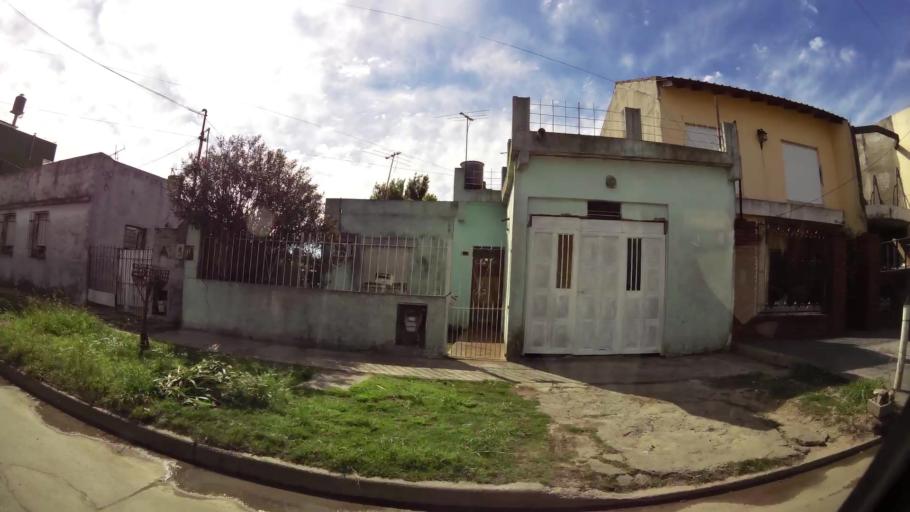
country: AR
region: Buenos Aires
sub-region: Partido de Almirante Brown
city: Adrogue
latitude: -34.7833
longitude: -58.3086
